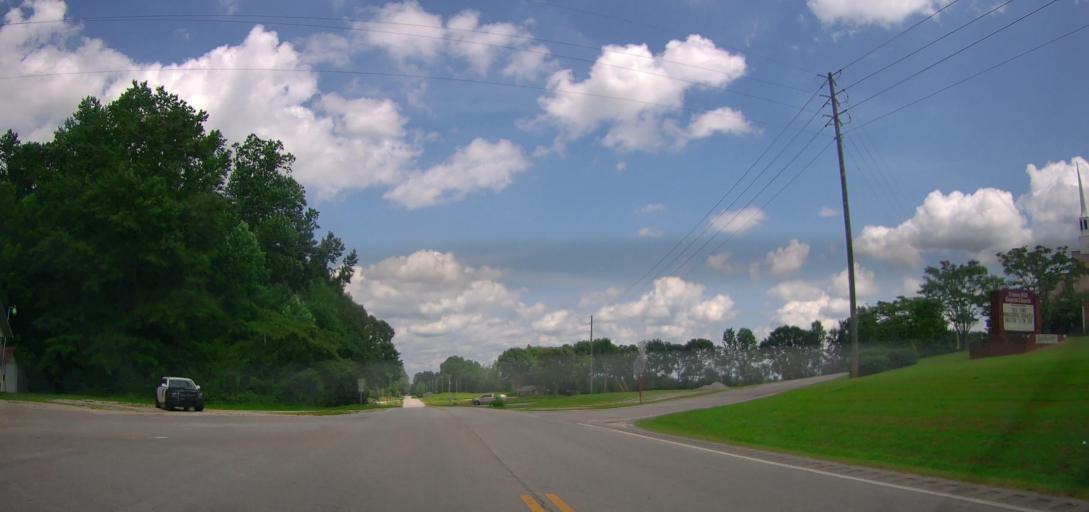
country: US
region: Georgia
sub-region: Carroll County
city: Bowdon
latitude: 33.5407
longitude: -85.3898
